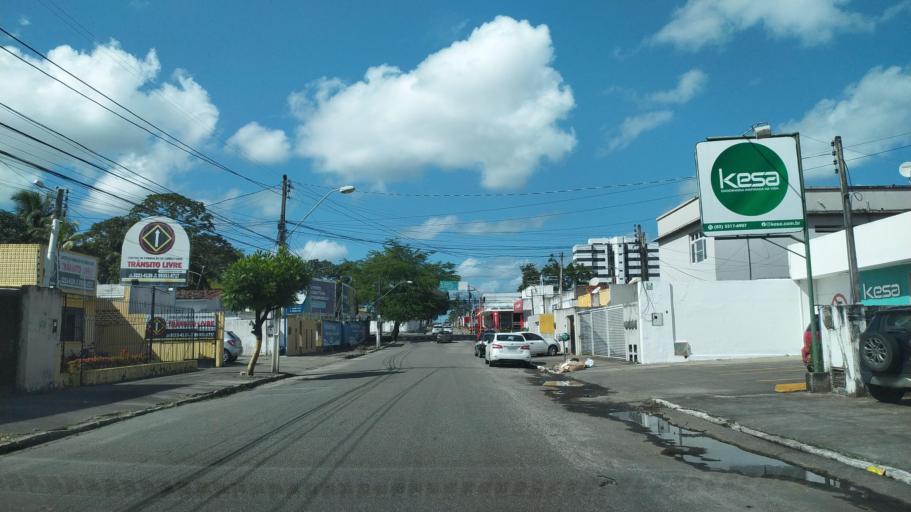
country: BR
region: Alagoas
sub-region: Maceio
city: Maceio
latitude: -9.6368
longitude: -35.7372
